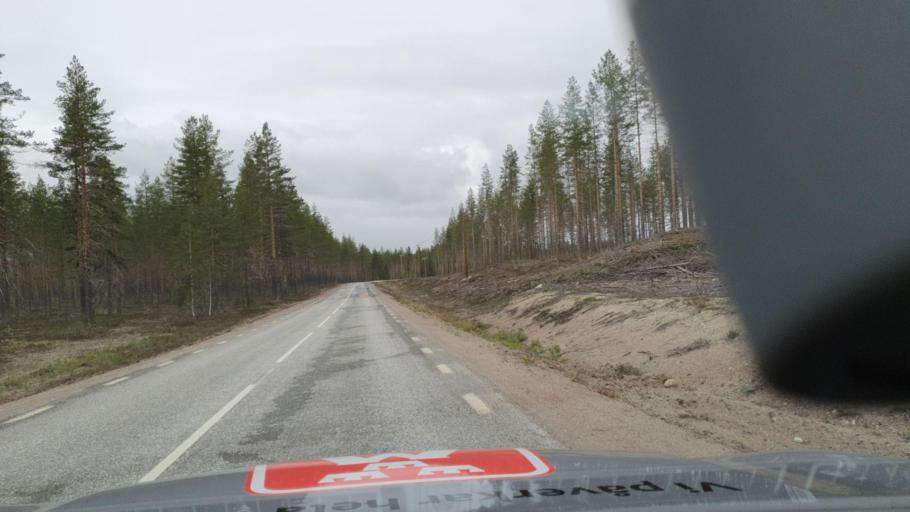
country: SE
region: Vaesternorrland
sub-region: Solleftea Kommun
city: Solleftea
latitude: 63.6333
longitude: 17.4293
